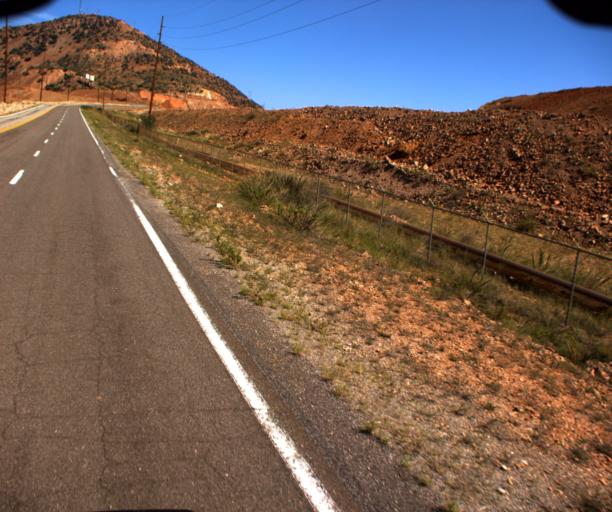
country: US
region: Arizona
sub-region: Greenlee County
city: Morenci
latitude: 33.0806
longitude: -109.3796
